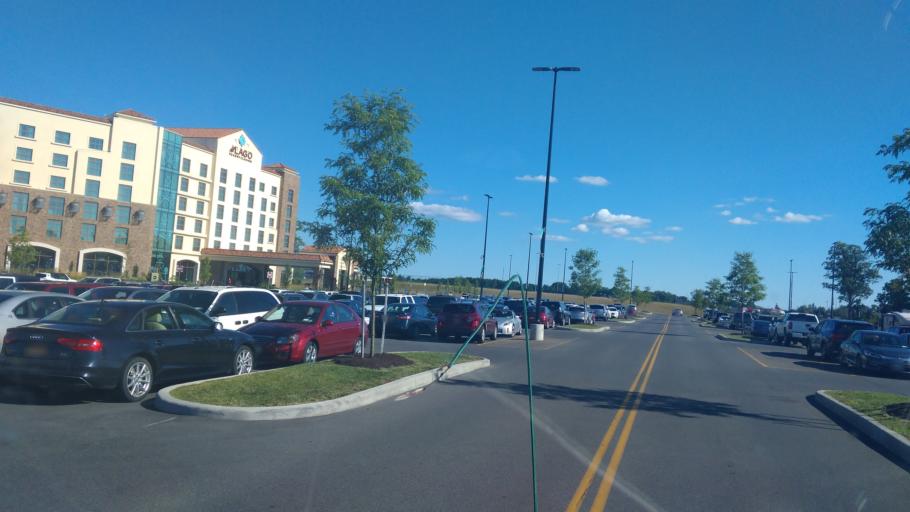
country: US
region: New York
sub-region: Seneca County
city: Waterloo
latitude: 42.9702
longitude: -76.8454
